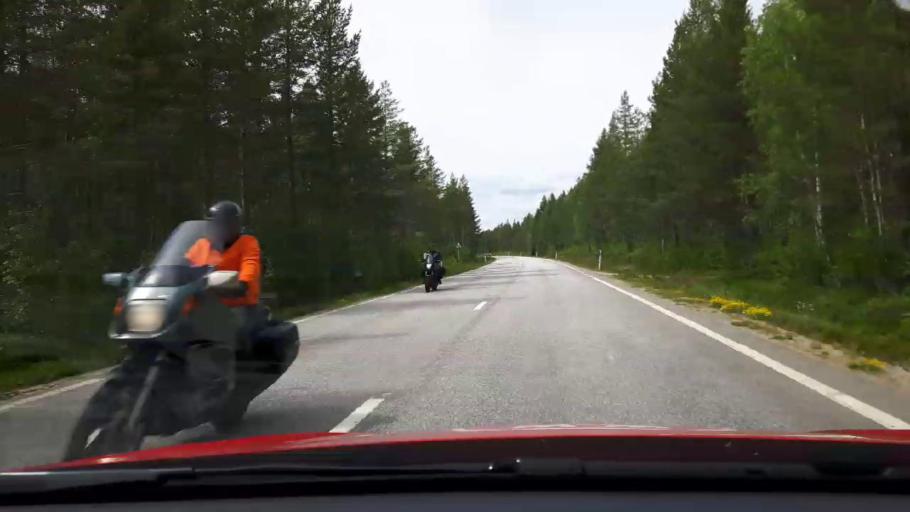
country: SE
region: Jaemtland
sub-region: Harjedalens Kommun
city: Sveg
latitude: 62.1254
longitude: 14.1477
